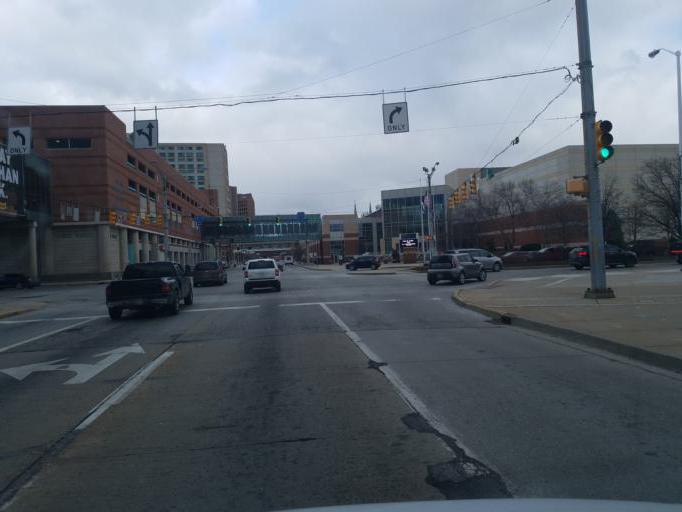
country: US
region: Indiana
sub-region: Marion County
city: Indianapolis
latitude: 39.7659
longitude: -86.1676
